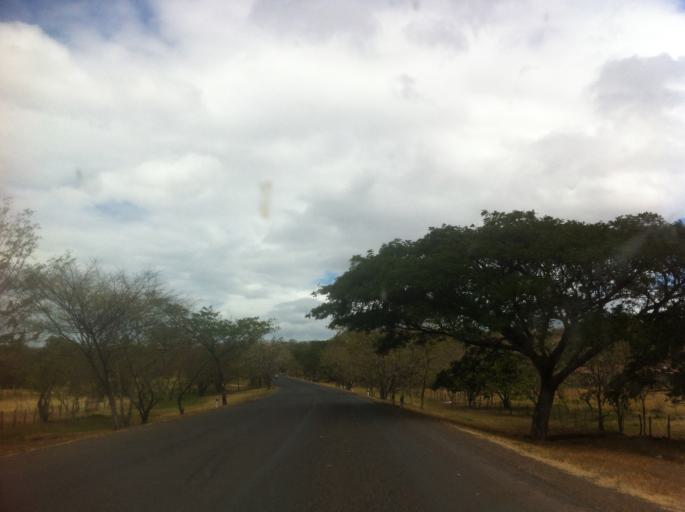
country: NI
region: Chontales
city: Juigalpa
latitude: 12.0818
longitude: -85.3239
